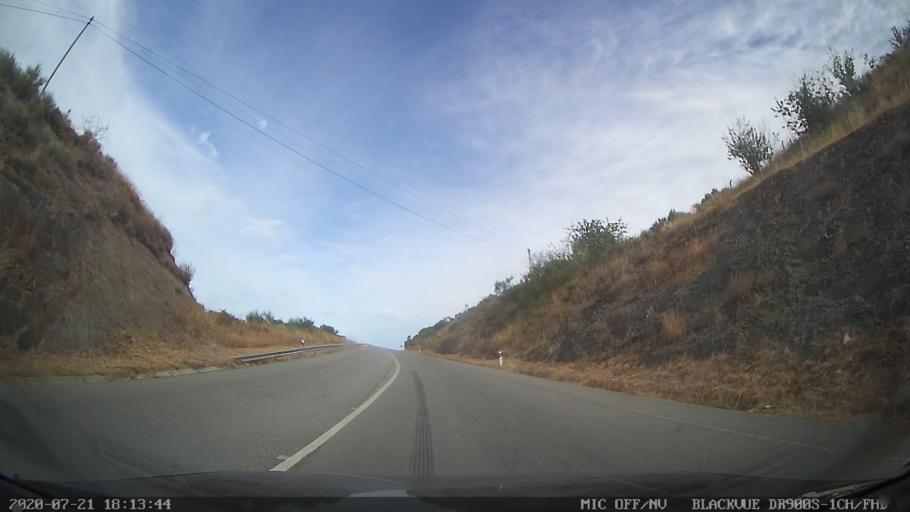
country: PT
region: Viseu
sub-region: Sao Joao da Pesqueira
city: Sao Joao da Pesqueira
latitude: 41.1280
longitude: -7.3969
